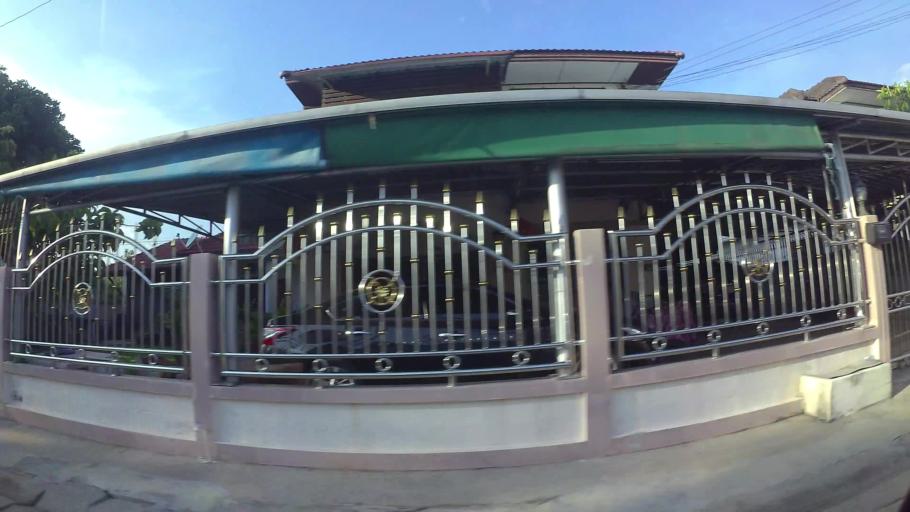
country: TH
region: Rayong
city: Rayong
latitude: 12.6811
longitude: 101.2906
